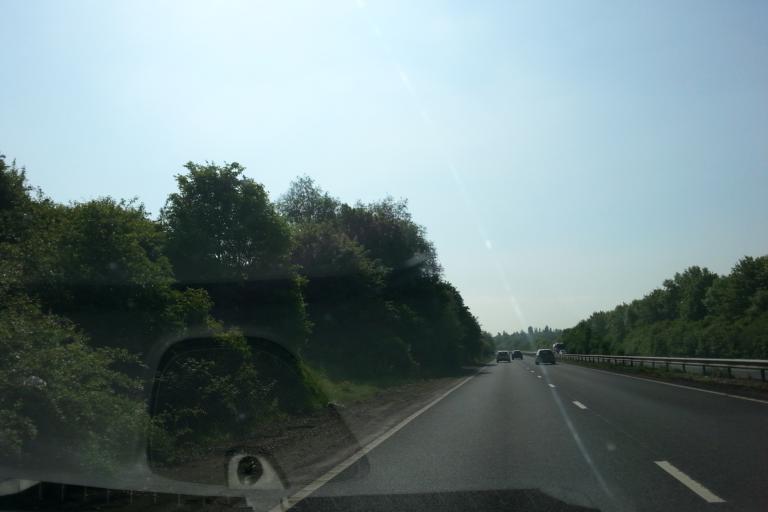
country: GB
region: England
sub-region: Peterborough
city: Castor
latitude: 52.5757
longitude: -0.3351
